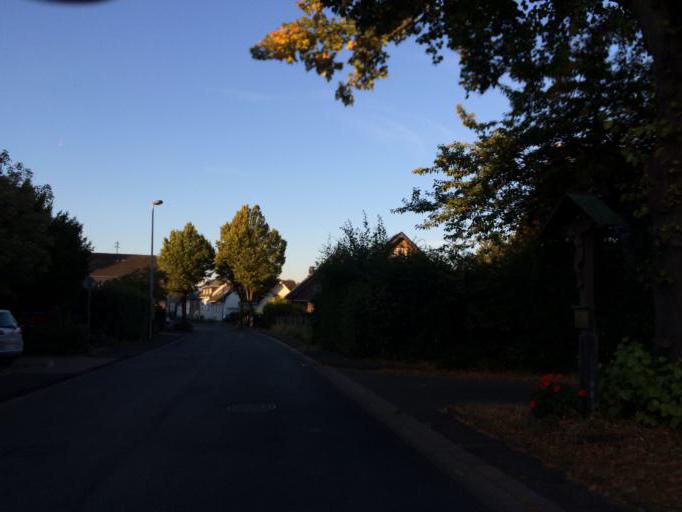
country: DE
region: North Rhine-Westphalia
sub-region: Regierungsbezirk Koln
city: Wachtberg
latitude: 50.6378
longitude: 7.1454
